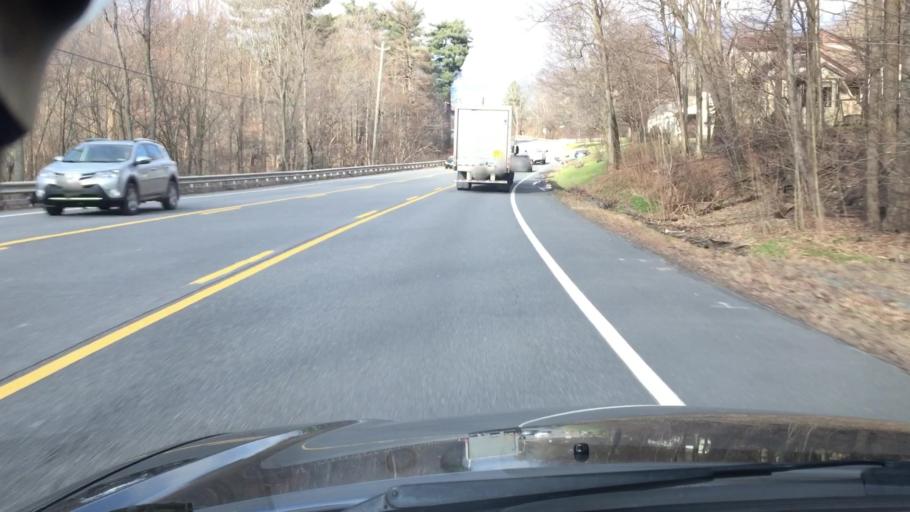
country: US
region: Pennsylvania
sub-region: Luzerne County
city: Dallas
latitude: 41.3397
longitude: -75.9589
